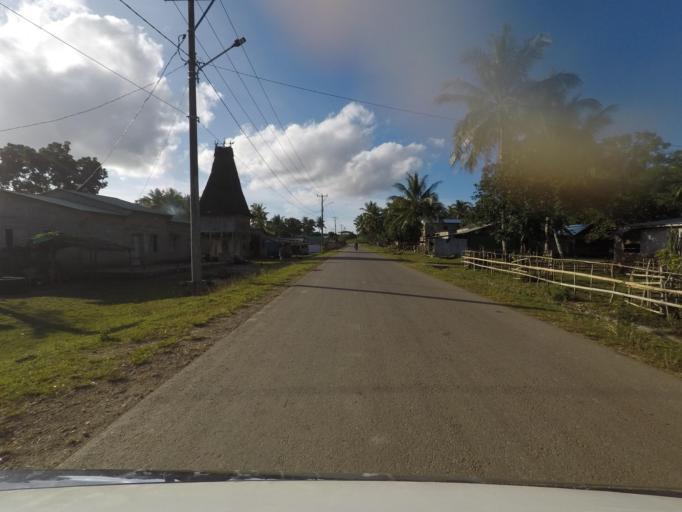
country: TL
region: Lautem
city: Lospalos
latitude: -8.4389
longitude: 127.0052
